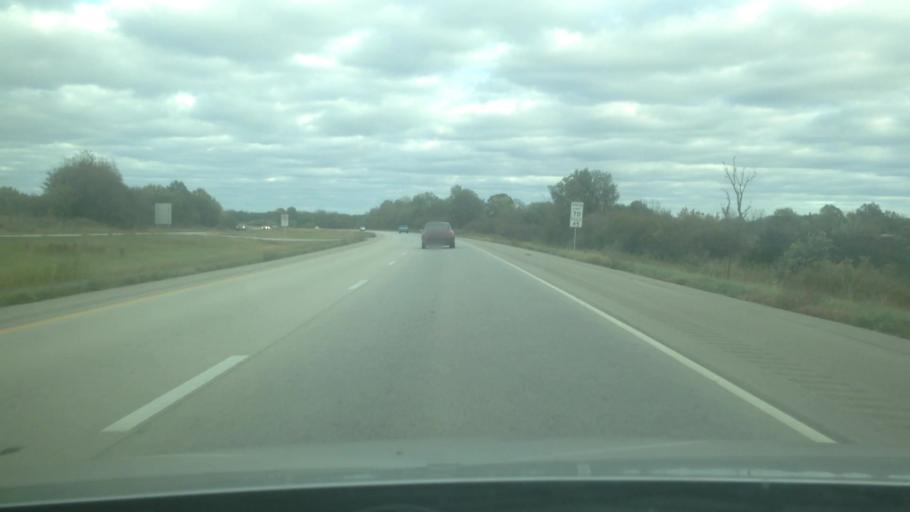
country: US
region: Illinois
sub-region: Macon County
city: Forsyth
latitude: 39.9106
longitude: -88.8802
